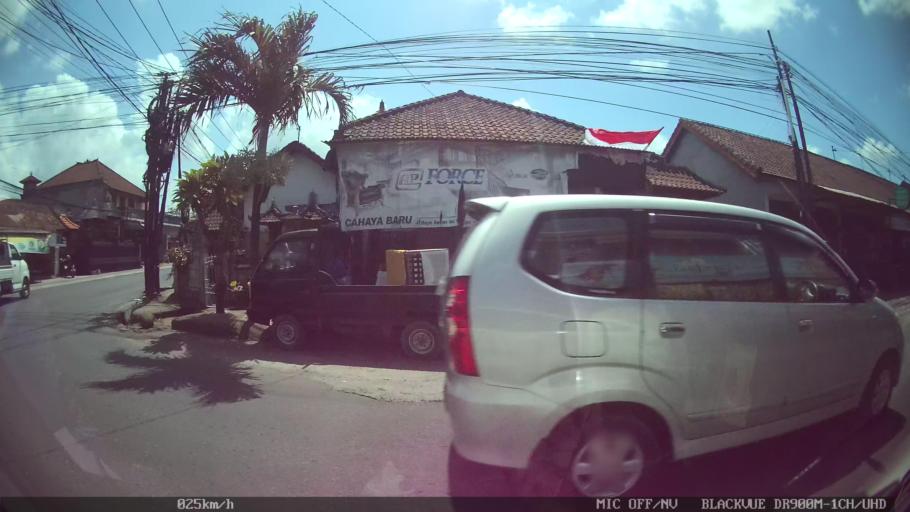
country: ID
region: Bali
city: Banjar Gunungpande
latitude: -8.6623
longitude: 115.1646
